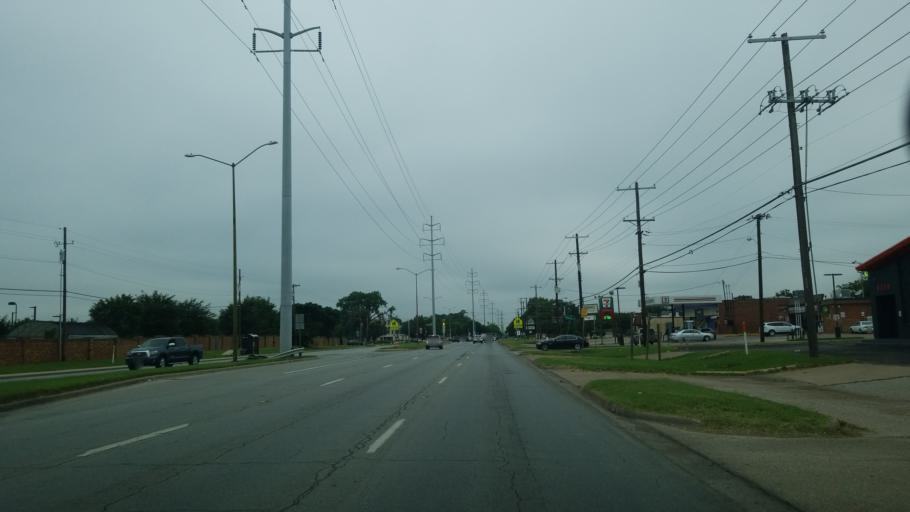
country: US
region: Texas
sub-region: Dallas County
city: University Park
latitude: 32.8356
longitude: -96.8632
